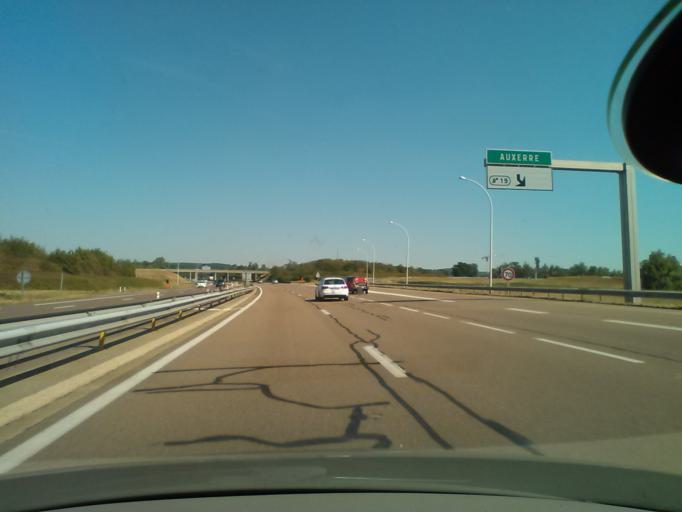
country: FR
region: Bourgogne
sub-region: Departement de l'Yonne
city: Gurgy
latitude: 47.8562
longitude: 3.5443
